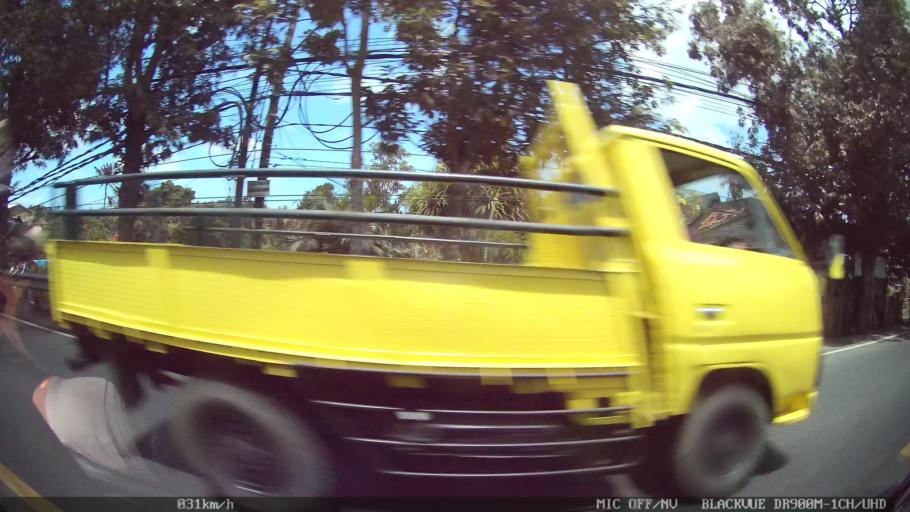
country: ID
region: Bali
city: Banjar Sedang
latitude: -8.5649
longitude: 115.2828
